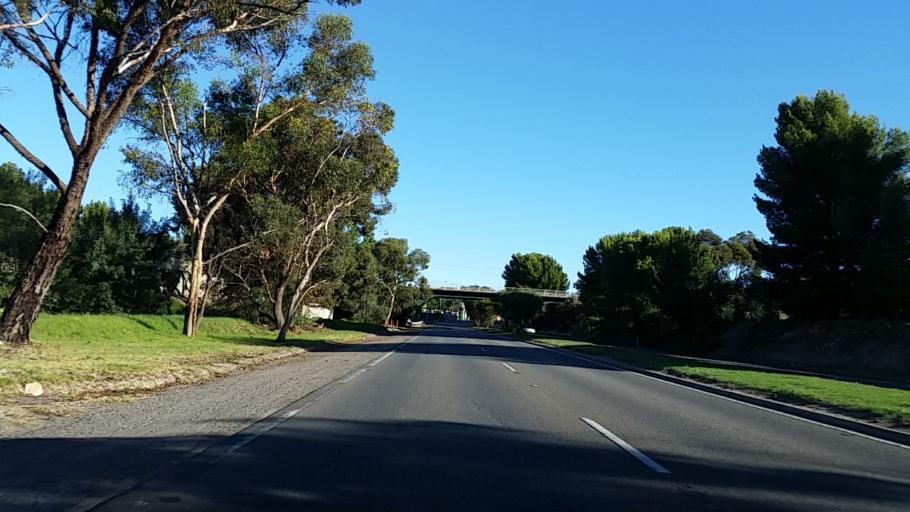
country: AU
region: South Australia
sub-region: Onkaparinga
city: Reynella
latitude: -35.0927
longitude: 138.5371
